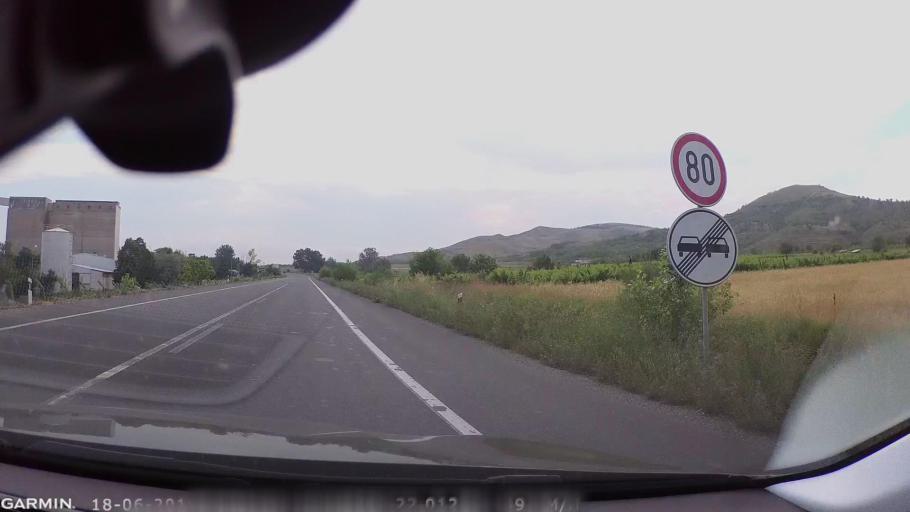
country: MK
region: Sveti Nikole
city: Sveti Nikole
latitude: 41.8041
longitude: 22.0163
